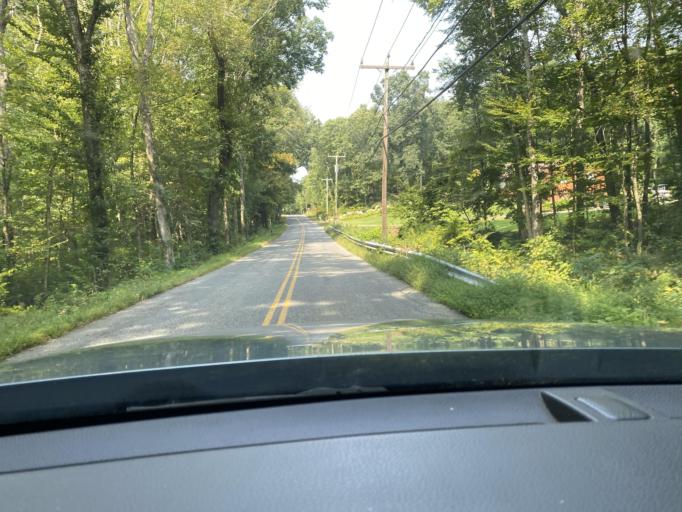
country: US
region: Connecticut
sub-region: Tolland County
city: Hebron
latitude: 41.6397
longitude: -72.2938
